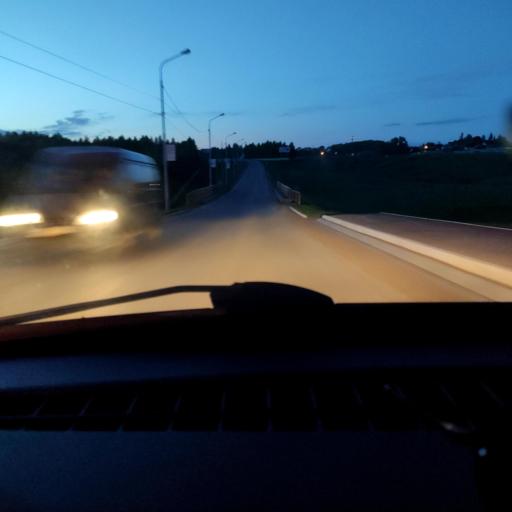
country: RU
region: Bashkortostan
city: Karmaskaly
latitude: 54.3731
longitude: 56.1734
